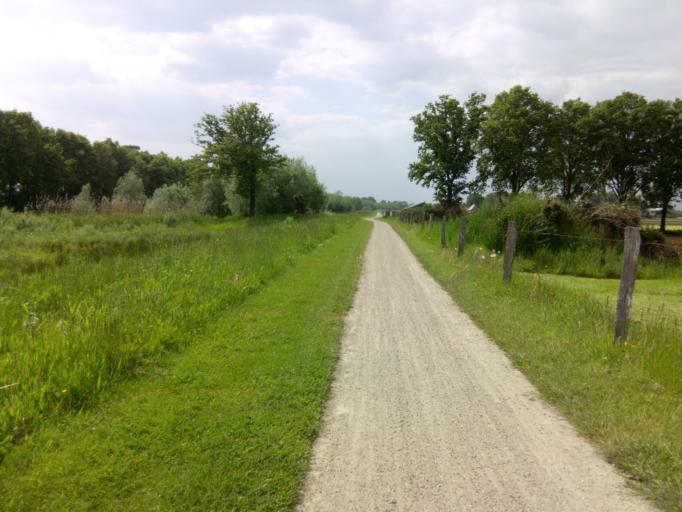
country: NL
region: Gelderland
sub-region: Oost Gelre
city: Lichtenvoorde
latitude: 52.0481
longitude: 6.5398
